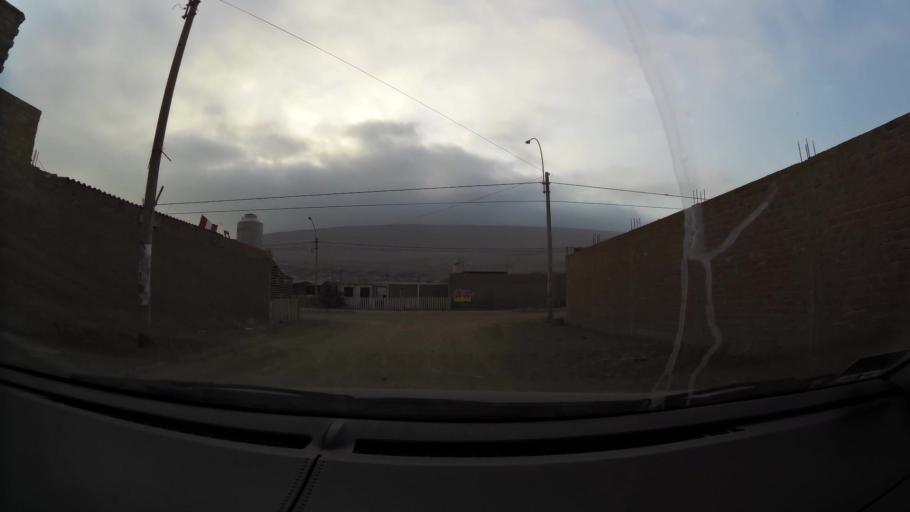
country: PE
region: Lima
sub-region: Lima
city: Santa Rosa
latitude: -11.7326
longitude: -77.1377
